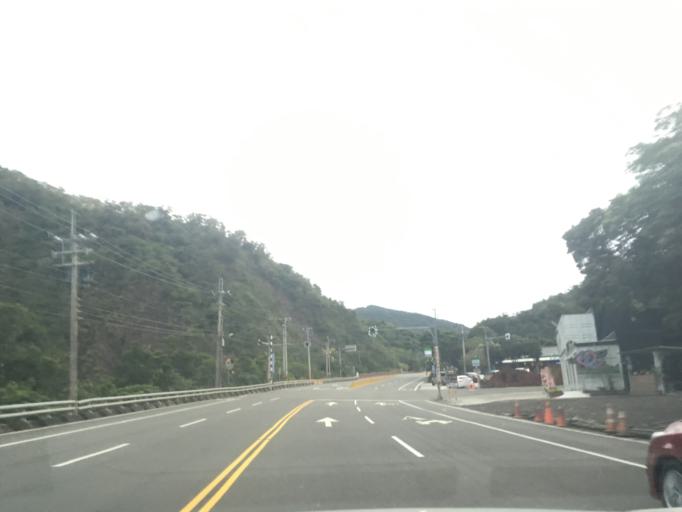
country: TW
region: Taiwan
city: Hengchun
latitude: 22.2181
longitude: 120.7935
